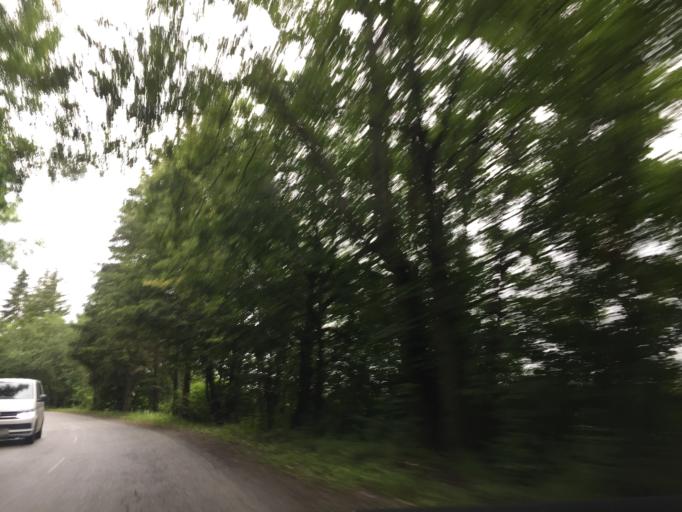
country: CZ
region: South Moravian
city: Ostrov u Macochy
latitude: 49.4003
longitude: 16.7634
